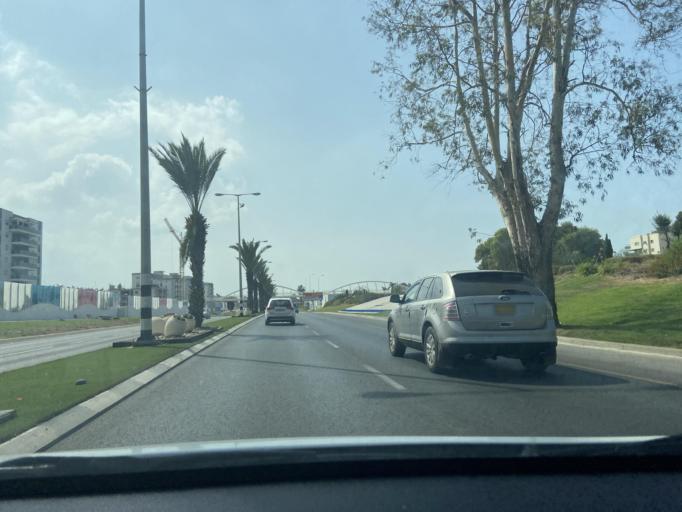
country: IL
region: Northern District
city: Nahariya
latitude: 33.0007
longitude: 35.0984
